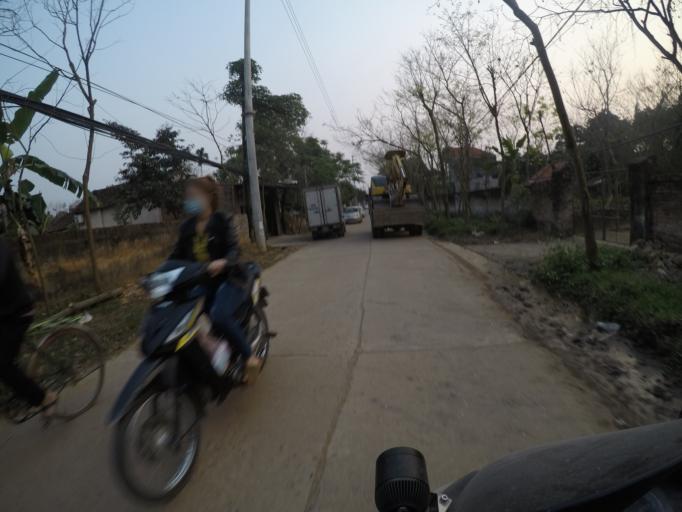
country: VN
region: Vinh Phuc
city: Trai Ngau
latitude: 21.4637
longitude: 105.5704
